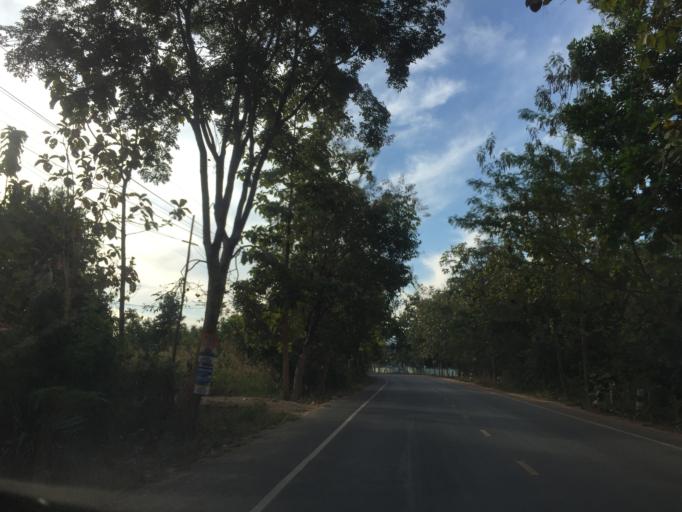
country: TH
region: Lamphun
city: Lamphun
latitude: 18.5097
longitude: 99.0293
